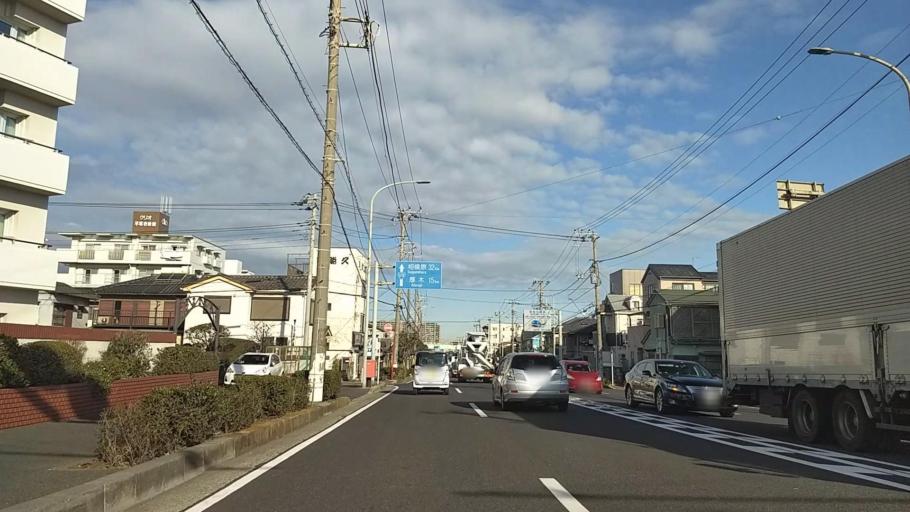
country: JP
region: Kanagawa
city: Hiratsuka
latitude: 35.3173
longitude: 139.3619
